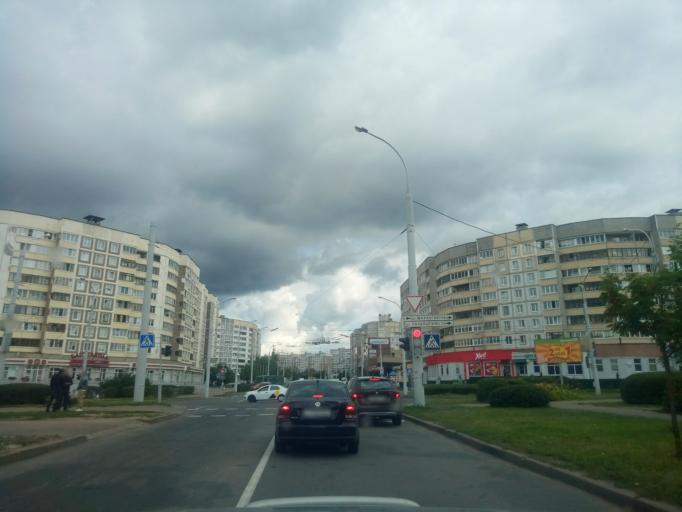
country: BY
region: Minsk
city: Novoye Medvezhino
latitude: 53.8818
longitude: 27.4396
